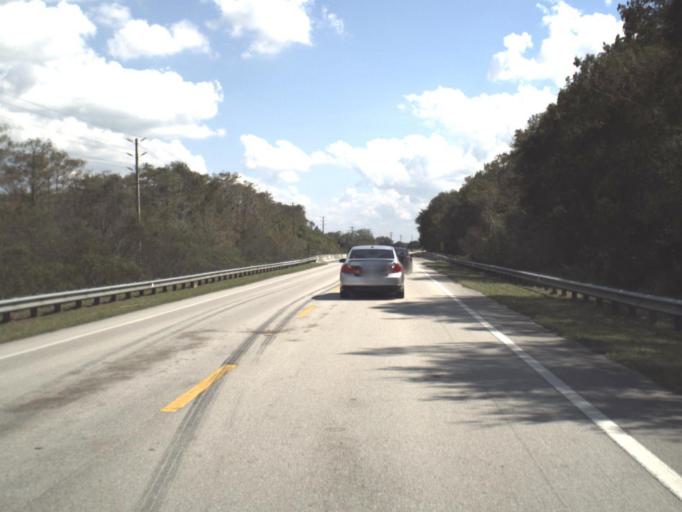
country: US
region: Florida
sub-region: Okeechobee County
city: Okeechobee
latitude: 27.3793
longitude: -80.9886
